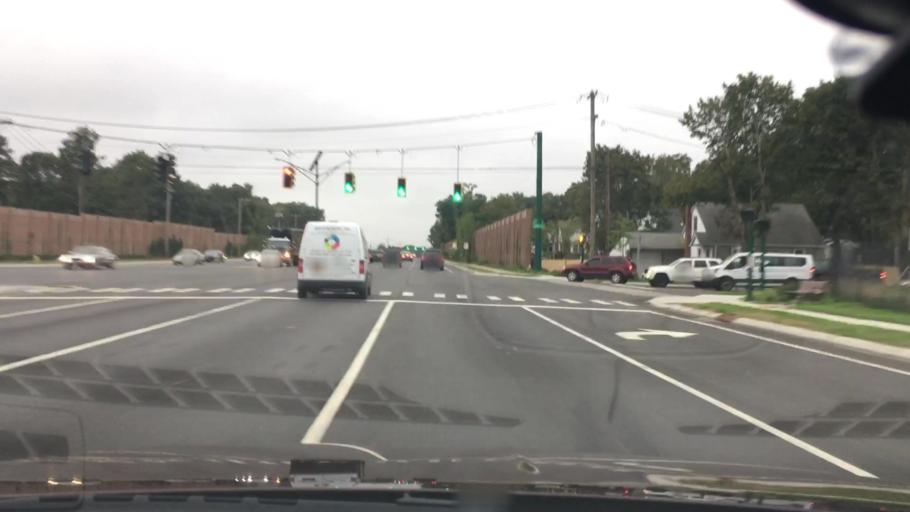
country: US
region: New York
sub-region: Suffolk County
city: Nesconset
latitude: 40.8525
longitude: -73.1536
